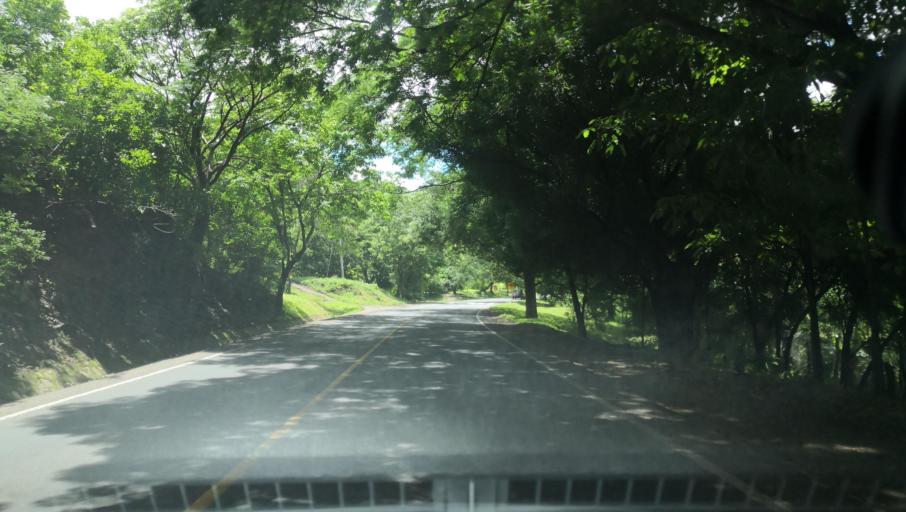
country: NI
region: Esteli
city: Condega
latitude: 13.3006
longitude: -86.3500
